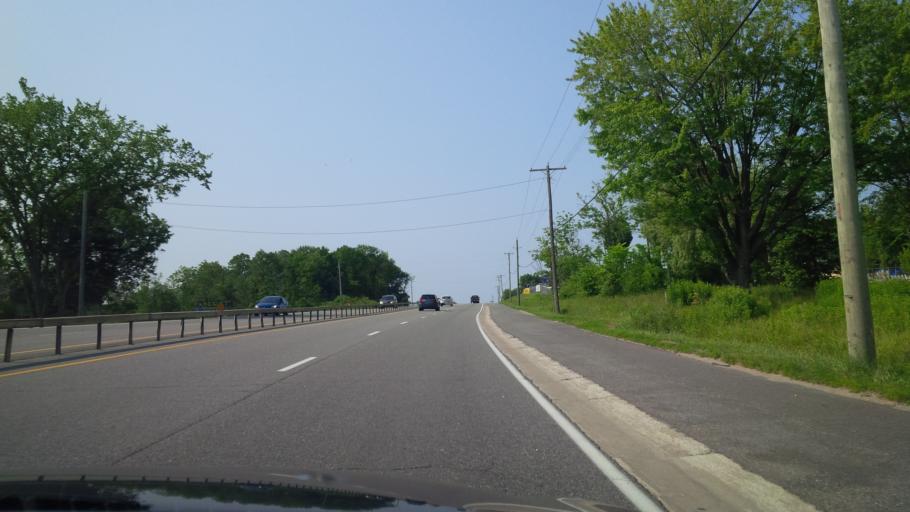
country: CA
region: Ontario
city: Orillia
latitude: 44.6664
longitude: -79.4124
